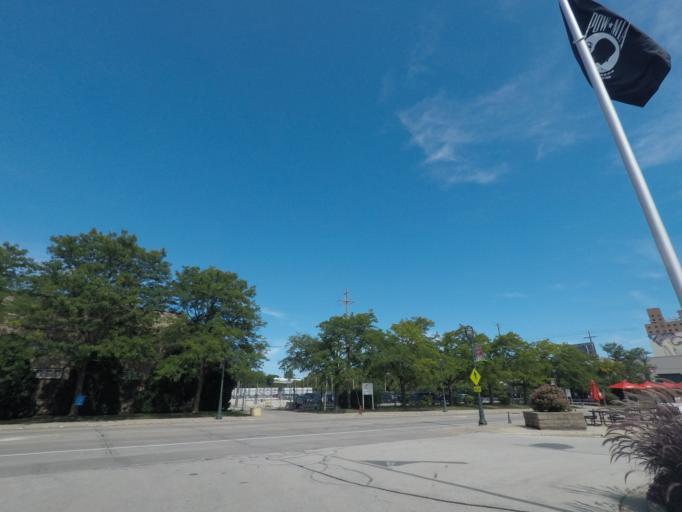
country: US
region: Wisconsin
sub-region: Milwaukee County
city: West Milwaukee
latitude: 43.0423
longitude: -87.9684
